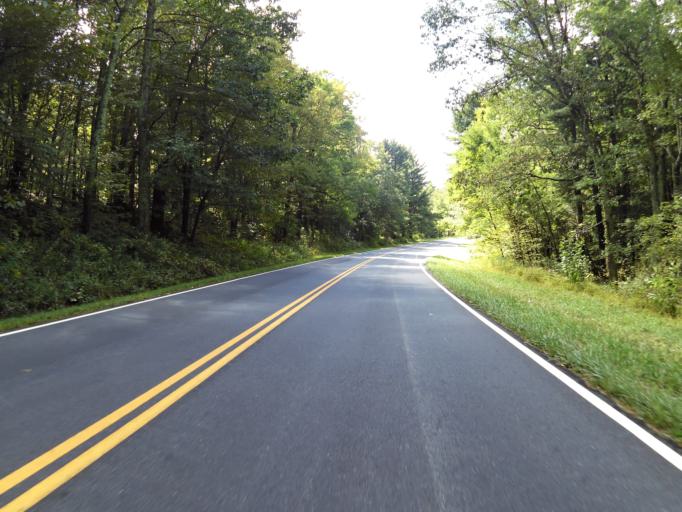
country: US
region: Virginia
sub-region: Rappahannock County
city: Washington
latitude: 38.7394
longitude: -78.3071
